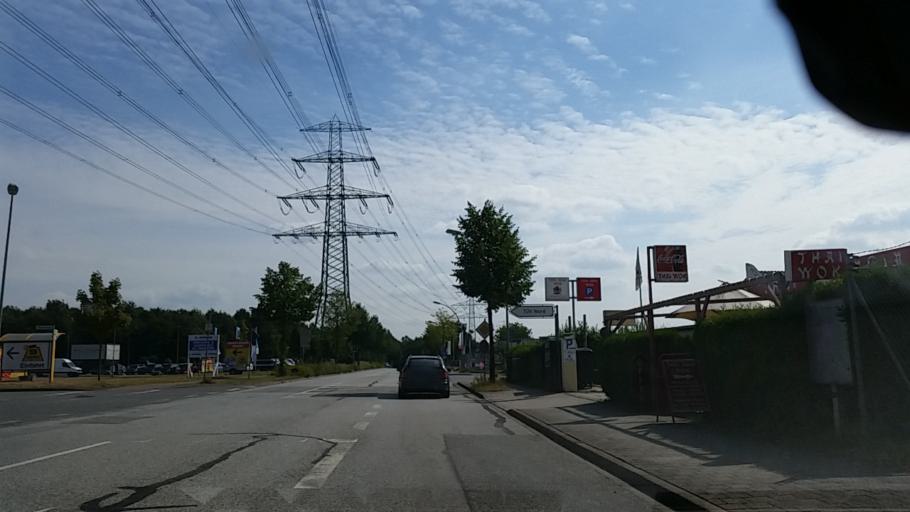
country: DE
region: Schleswig-Holstein
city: Wentorf bei Hamburg
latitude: 53.4878
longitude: 10.2626
